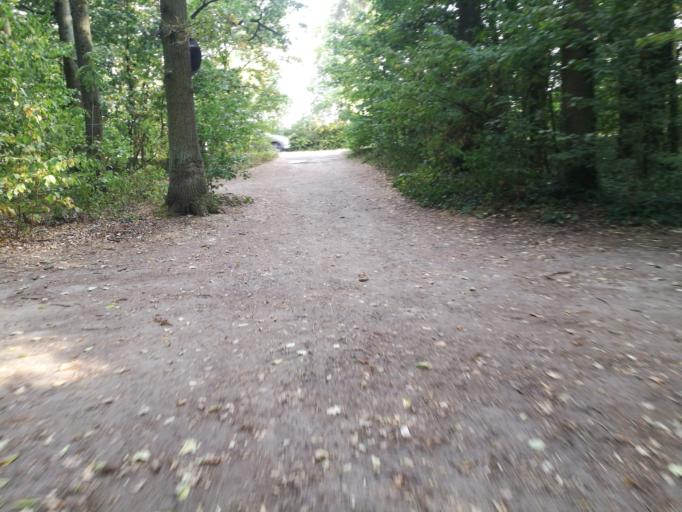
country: DE
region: Bavaria
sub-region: Regierungsbezirk Mittelfranken
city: Seukendorf
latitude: 49.4881
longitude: 10.9098
